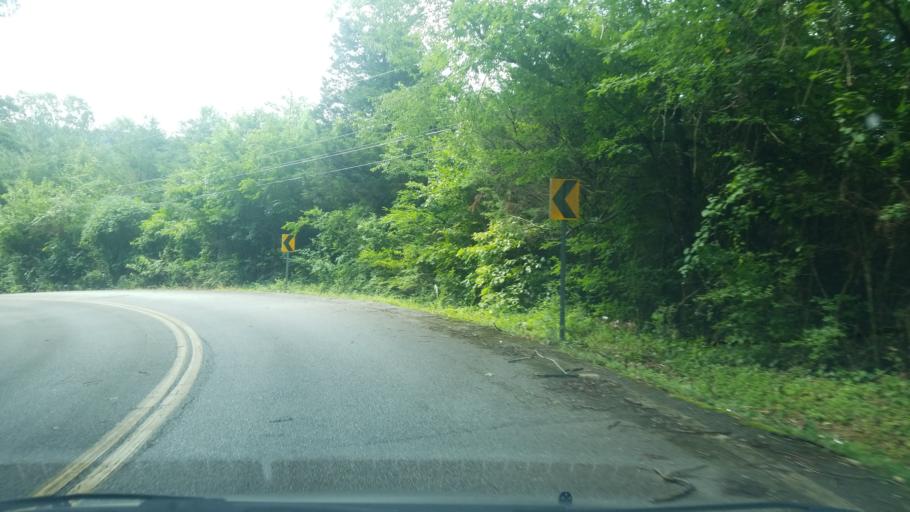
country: US
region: Tennessee
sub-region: Hamilton County
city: Apison
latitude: 35.0097
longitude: -85.0518
